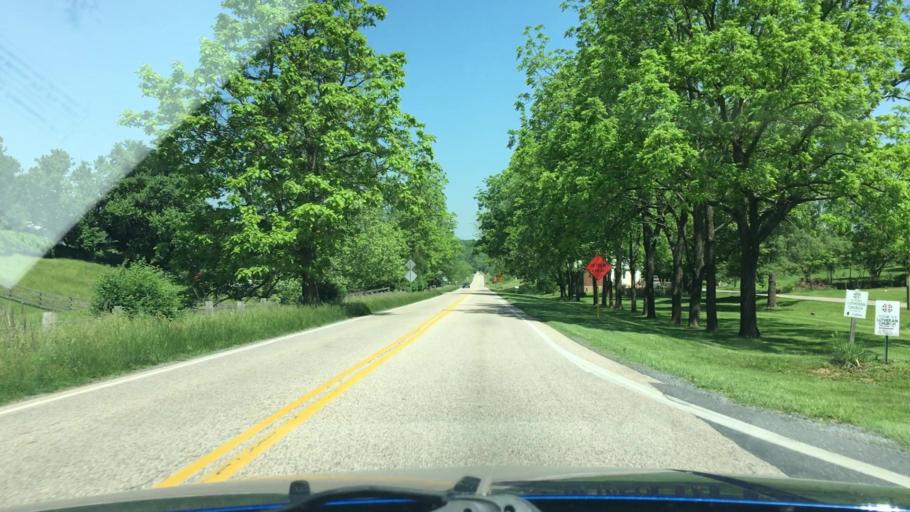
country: US
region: Virginia
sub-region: City of Staunton
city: Staunton
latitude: 38.1959
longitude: -79.1142
